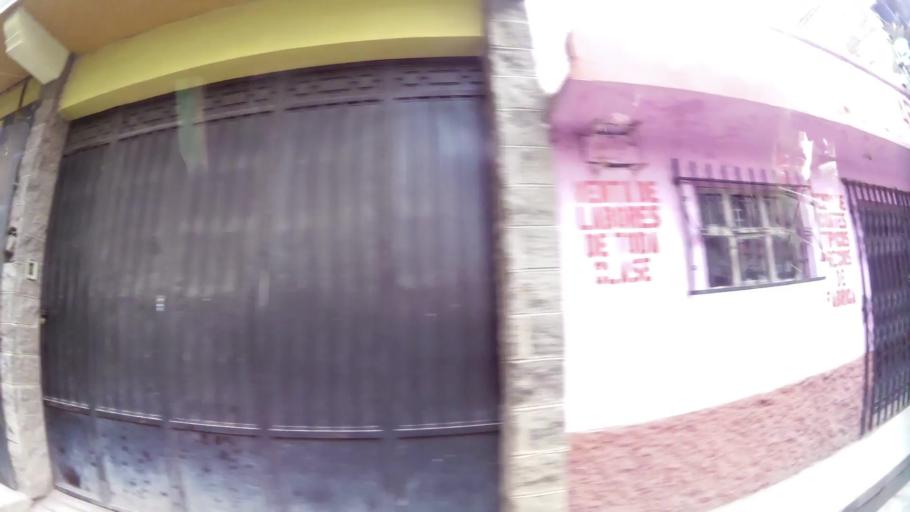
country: GT
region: Quetzaltenango
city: Salcaja
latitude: 14.8800
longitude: -91.4573
